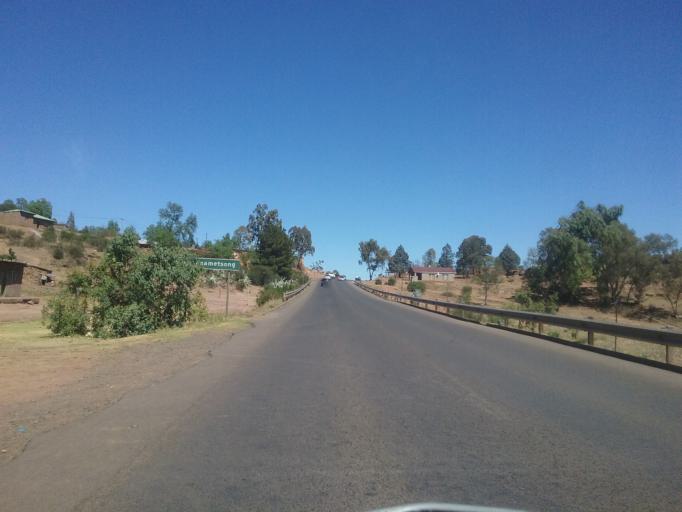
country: LS
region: Quthing
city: Quthing
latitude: -30.3985
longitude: 27.6683
